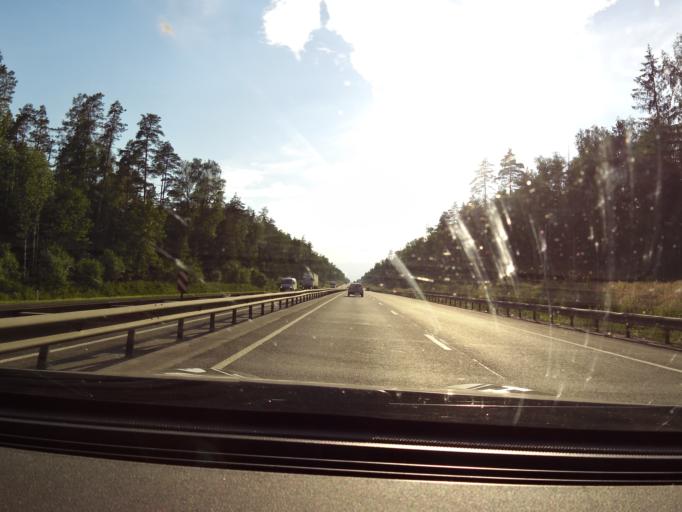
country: RU
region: Vladimir
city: Krasnyy Oktyabr'
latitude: 56.2160
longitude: 41.4053
